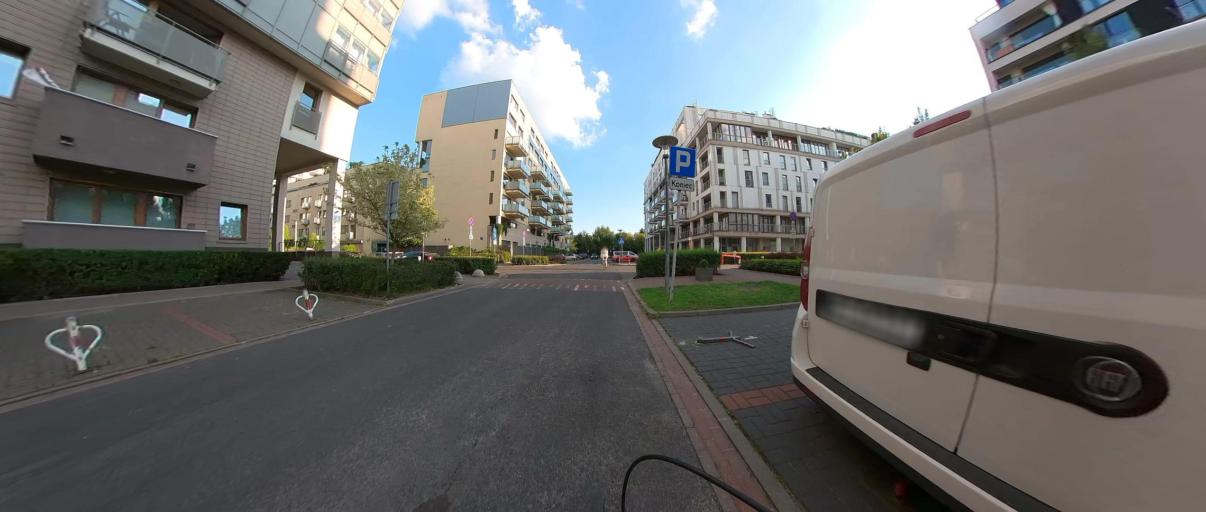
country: PL
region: Masovian Voivodeship
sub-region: Warszawa
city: Ochota
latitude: 52.2026
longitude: 20.9959
